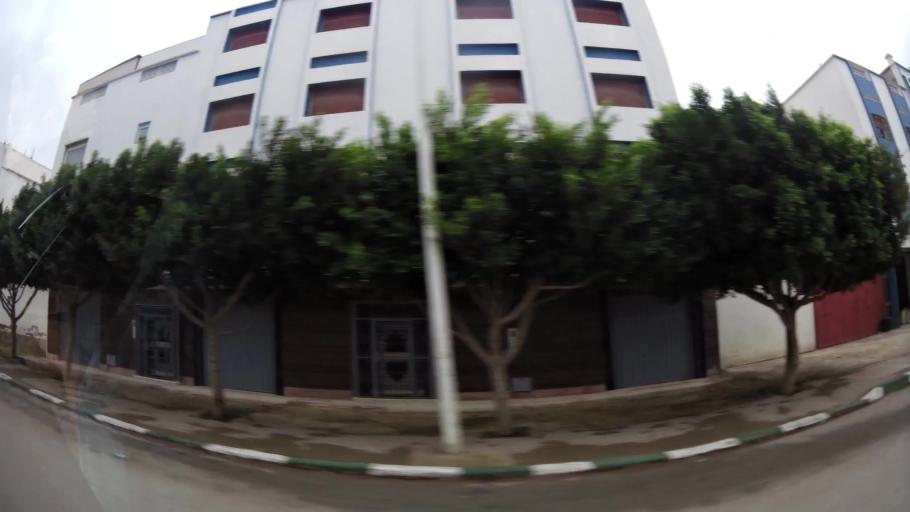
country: MA
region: Oriental
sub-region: Nador
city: Midar
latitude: 35.0521
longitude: -3.4611
